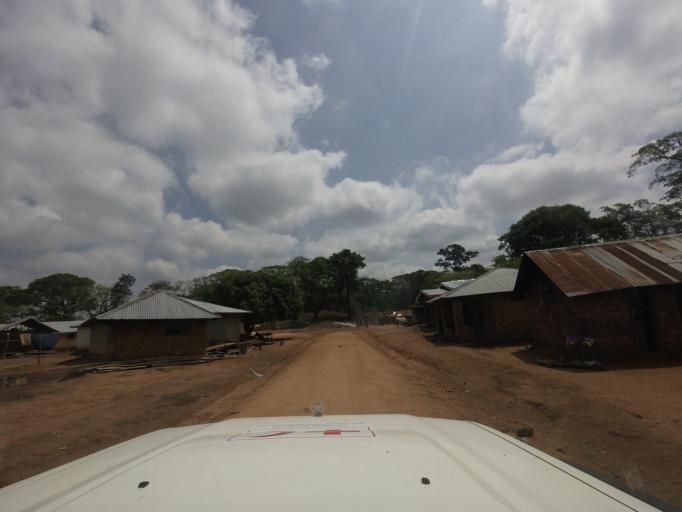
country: LR
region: Lofa
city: Voinjama
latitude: 8.4574
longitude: -9.6411
